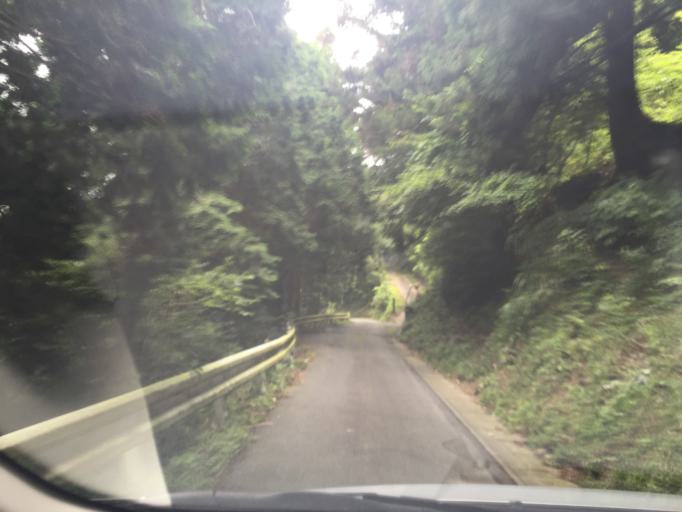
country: JP
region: Shizuoka
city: Kanaya
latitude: 34.8393
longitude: 138.0688
